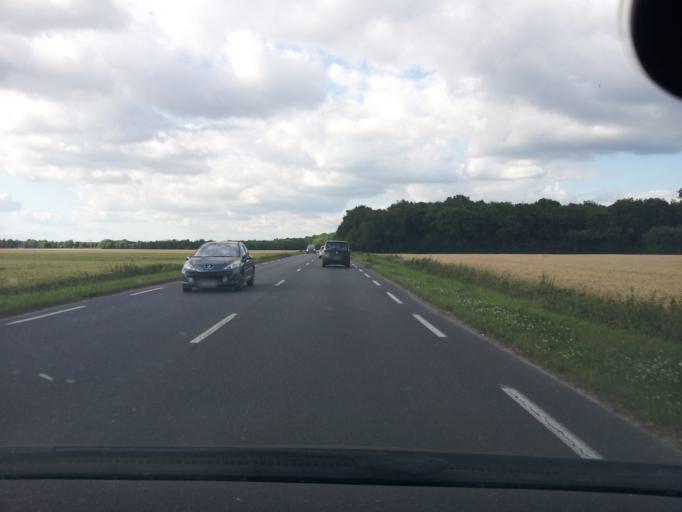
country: FR
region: Ile-de-France
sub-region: Departement de l'Essonne
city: Vert-le-Grand
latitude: 48.5878
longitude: 2.3684
